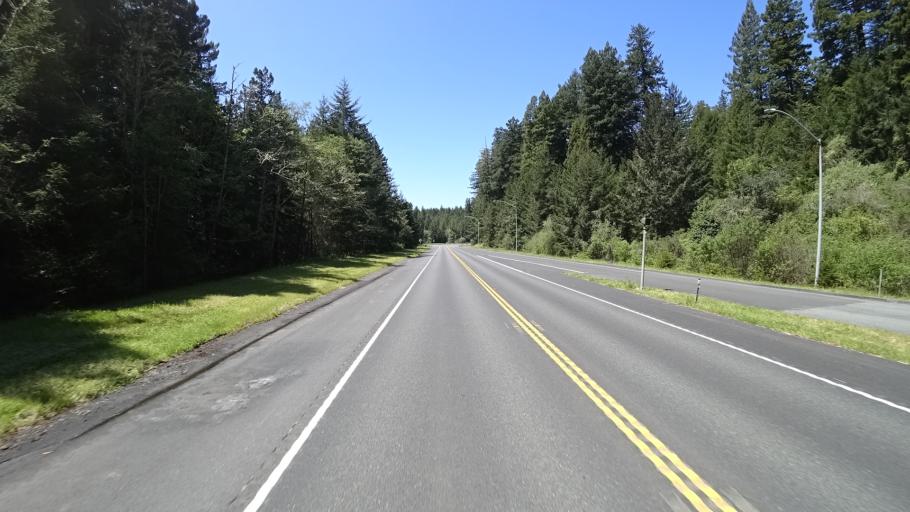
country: US
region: California
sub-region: Humboldt County
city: Blue Lake
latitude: 40.8841
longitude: -123.9647
